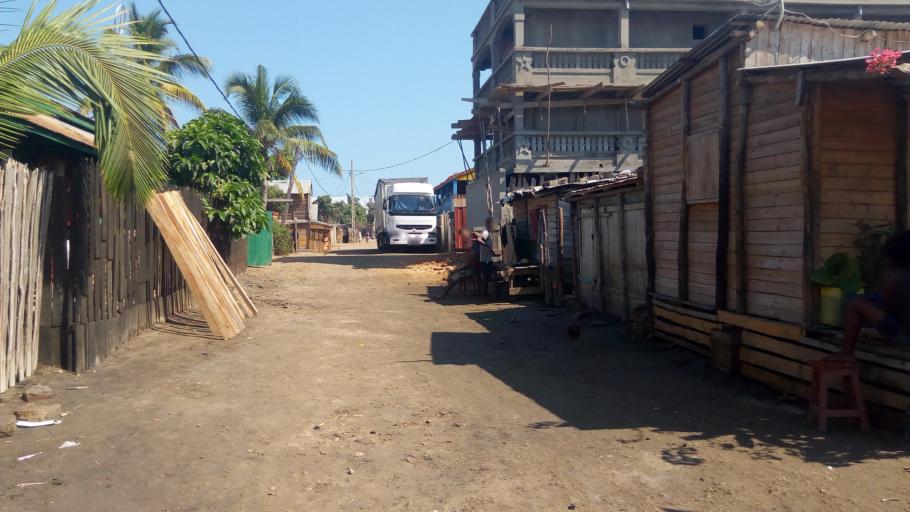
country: MG
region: Menabe
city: Morondava
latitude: -20.2981
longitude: 44.2815
